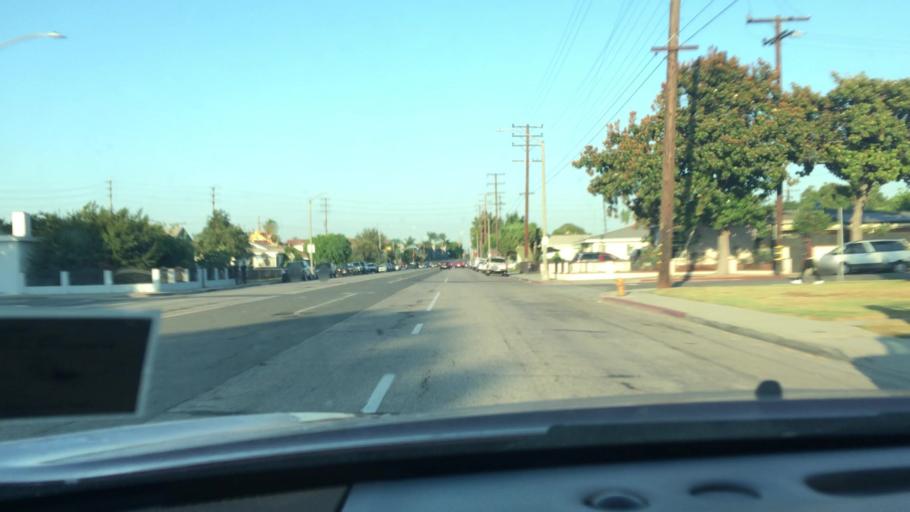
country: US
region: California
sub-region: Los Angeles County
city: Paramount
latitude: 33.8543
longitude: -118.1709
